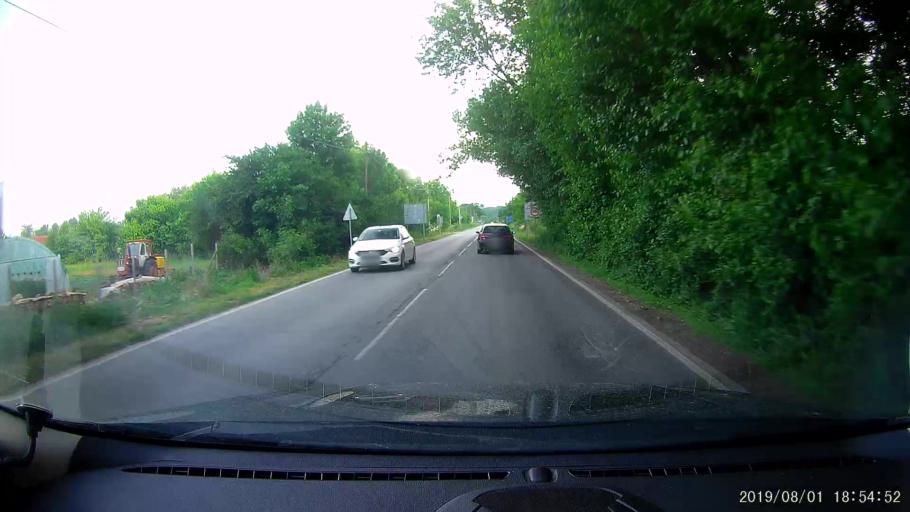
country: BG
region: Shumen
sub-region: Obshtina Shumen
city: Shumen
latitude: 43.1897
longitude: 27.0033
